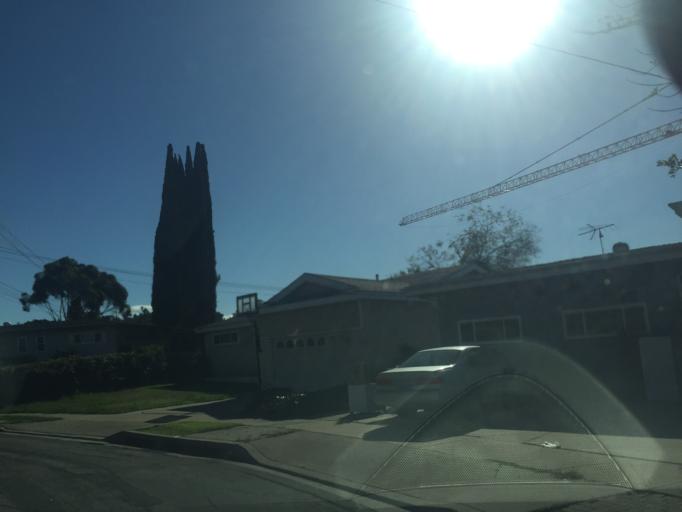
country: US
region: California
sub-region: San Diego County
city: La Mesa
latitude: 32.7842
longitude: -117.0956
